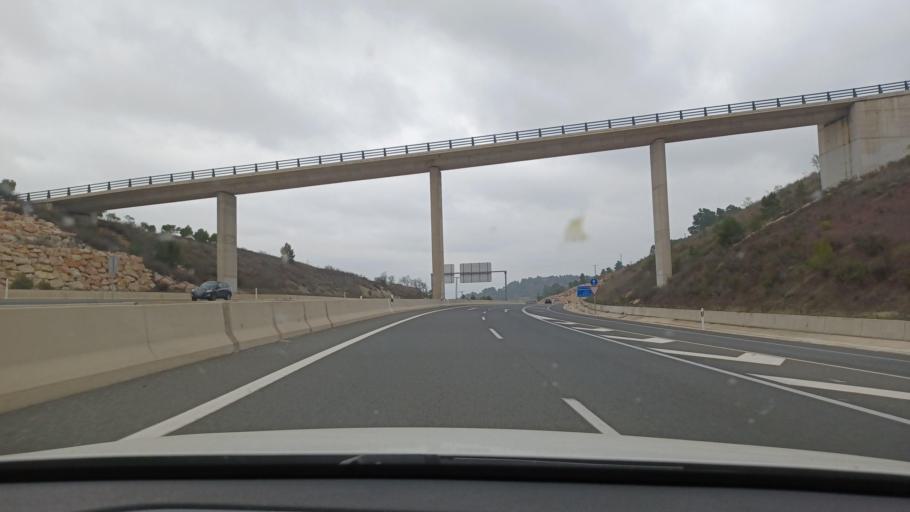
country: ES
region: Valencia
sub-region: Provincia de Alicante
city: Alcoy
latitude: 38.6862
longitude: -0.4602
